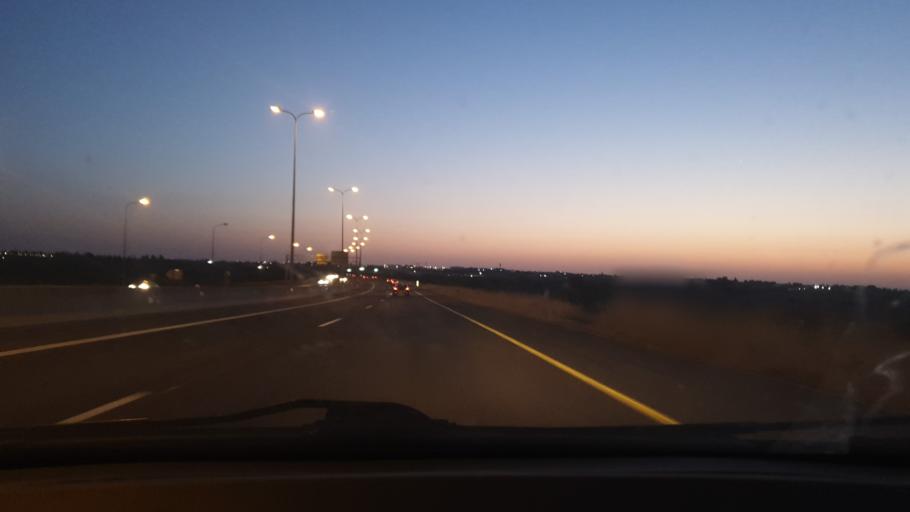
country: IL
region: Central District
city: Gedera
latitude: 31.8055
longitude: 34.8254
